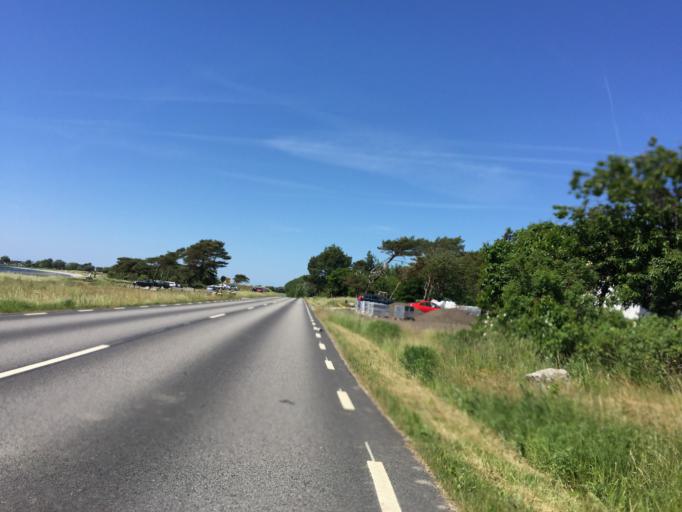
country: SE
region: Skane
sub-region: Trelleborgs Kommun
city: Skare
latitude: 55.3733
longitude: 13.0677
